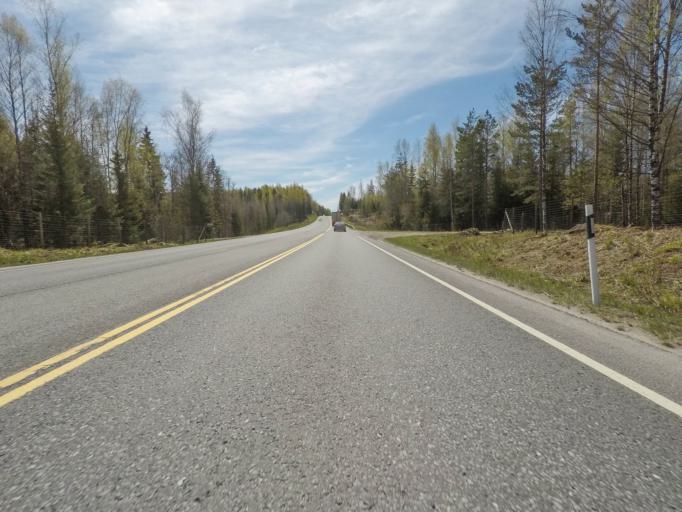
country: FI
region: Pirkanmaa
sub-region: Etelae-Pirkanmaa
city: Urjala
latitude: 61.0400
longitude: 23.5015
